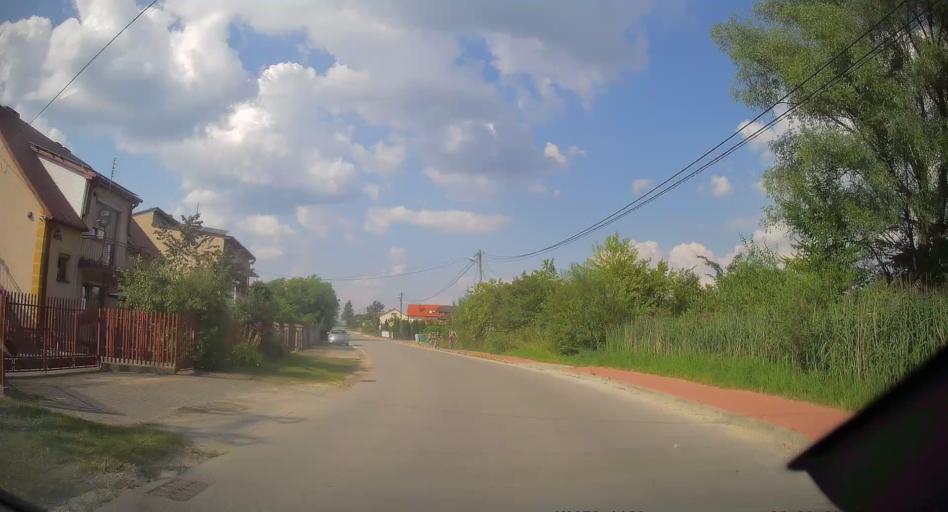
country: PL
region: Swietokrzyskie
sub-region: Powiat konecki
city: Radoszyce
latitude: 51.0799
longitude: 20.2574
